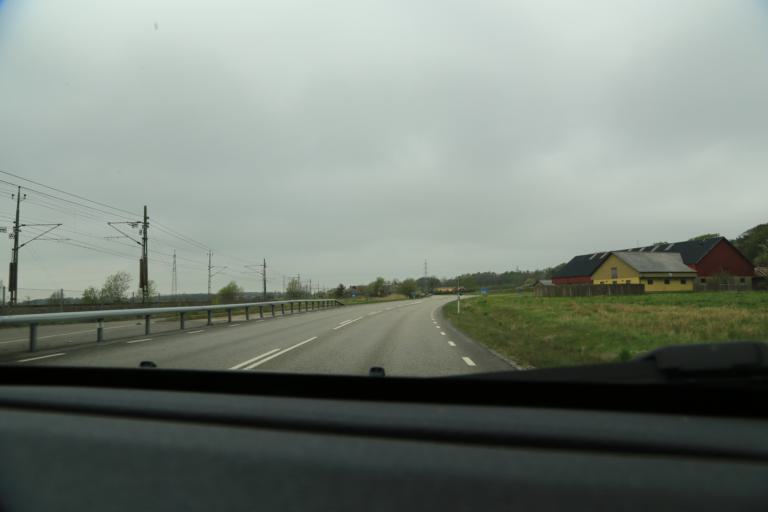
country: SE
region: Halland
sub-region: Kungsbacka Kommun
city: Frillesas
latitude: 57.2322
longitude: 12.2065
